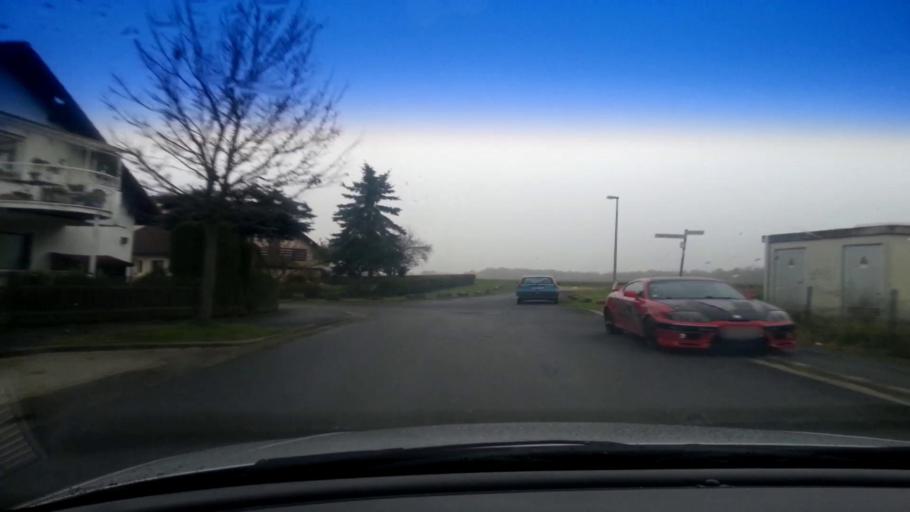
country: DE
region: Bavaria
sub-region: Upper Franconia
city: Gundelsheim
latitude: 49.9415
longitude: 10.9135
